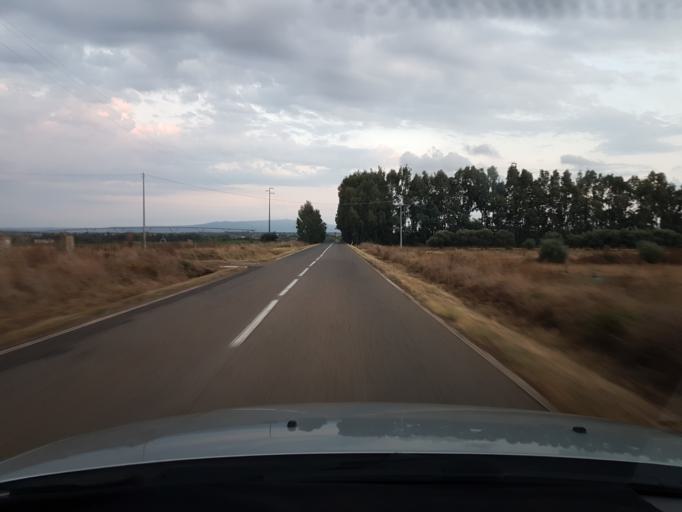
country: IT
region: Sardinia
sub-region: Provincia di Oristano
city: Tramatza
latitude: 40.0222
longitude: 8.6421
